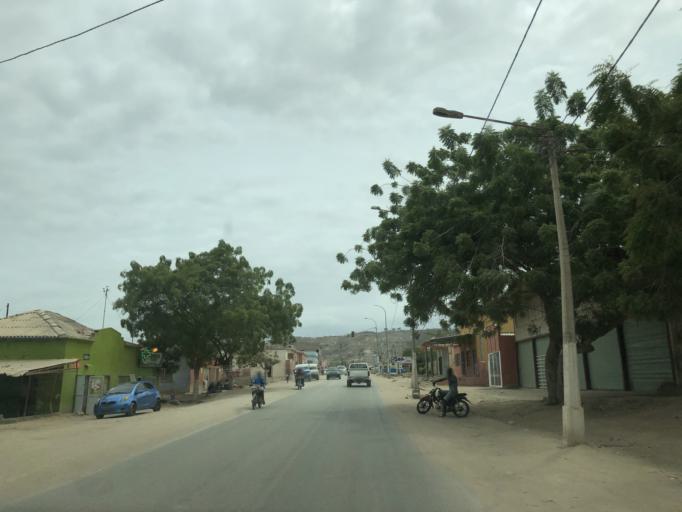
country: AO
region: Cuanza Sul
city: Sumbe
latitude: -11.1829
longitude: 13.8627
